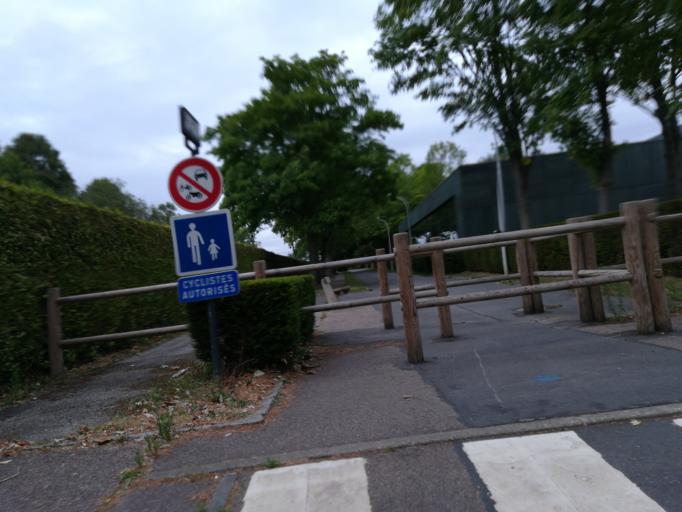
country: FR
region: Haute-Normandie
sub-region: Departement de la Seine-Maritime
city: Mont-Saint-Aignan
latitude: 49.4648
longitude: 1.0745
